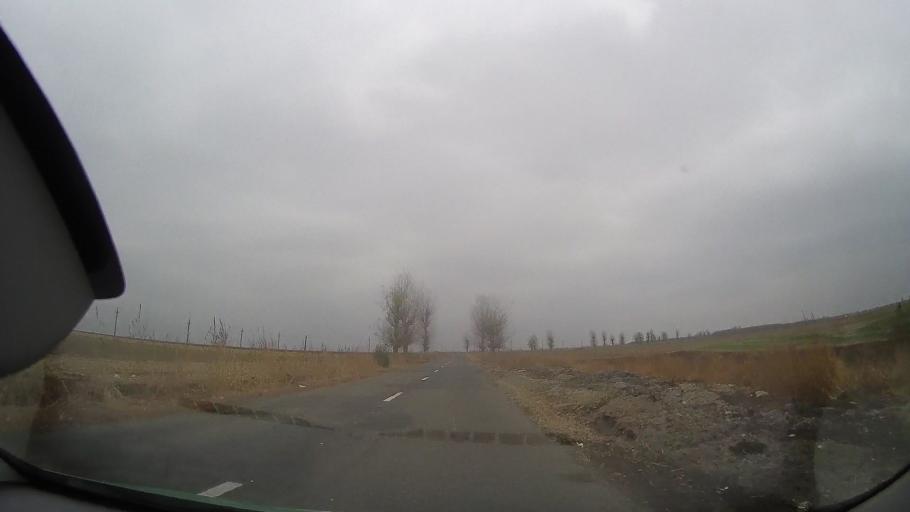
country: RO
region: Ialomita
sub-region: Comuna Grindu
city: Grindu
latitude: 44.7932
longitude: 26.8960
